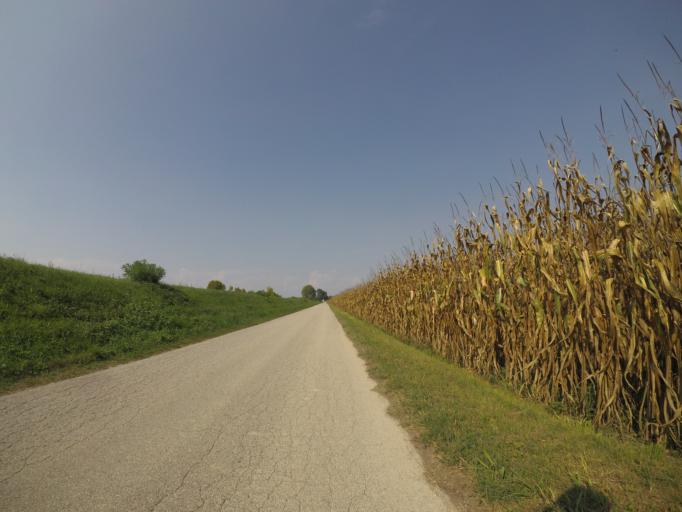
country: IT
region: Friuli Venezia Giulia
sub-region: Provincia di Udine
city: Camino al Tagliamento
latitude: 45.9413
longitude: 12.9186
